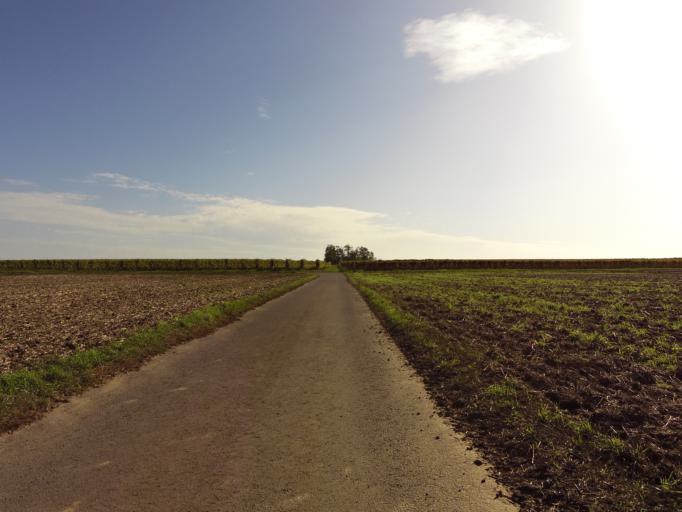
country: DE
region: Rheinland-Pfalz
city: Hohen-Sulzen
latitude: 49.6245
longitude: 8.2217
